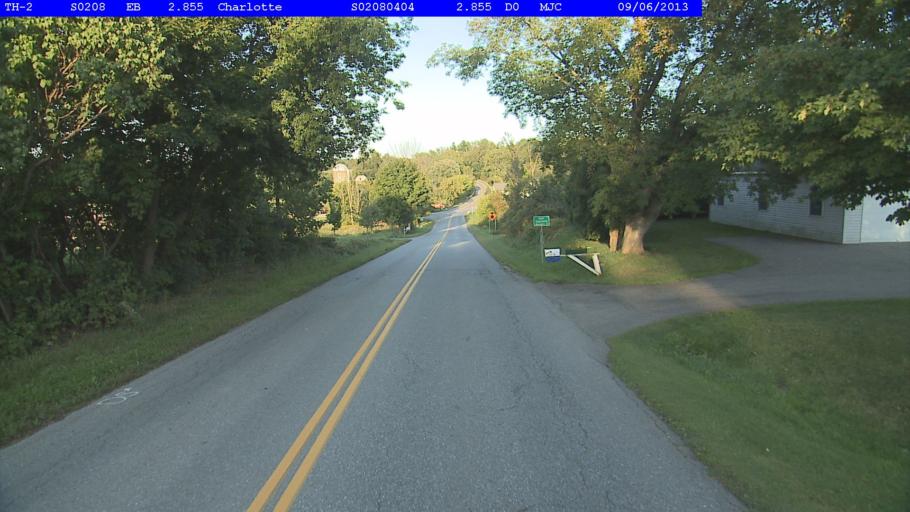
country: US
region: Vermont
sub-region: Chittenden County
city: Hinesburg
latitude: 44.3195
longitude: -73.1914
